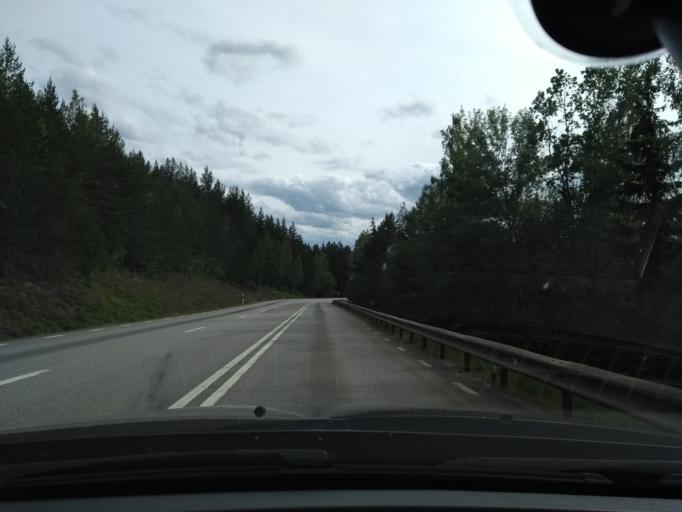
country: SE
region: Joenkoeping
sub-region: Eksjo Kommun
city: Mariannelund
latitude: 57.6304
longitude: 15.6190
